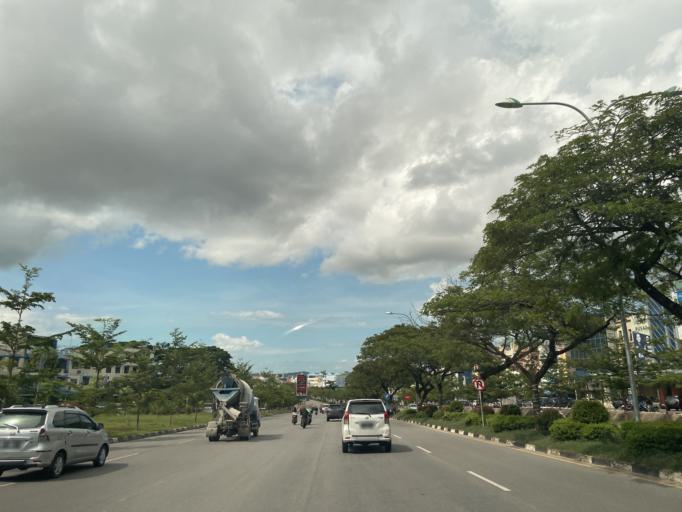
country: SG
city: Singapore
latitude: 1.1276
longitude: 104.0343
